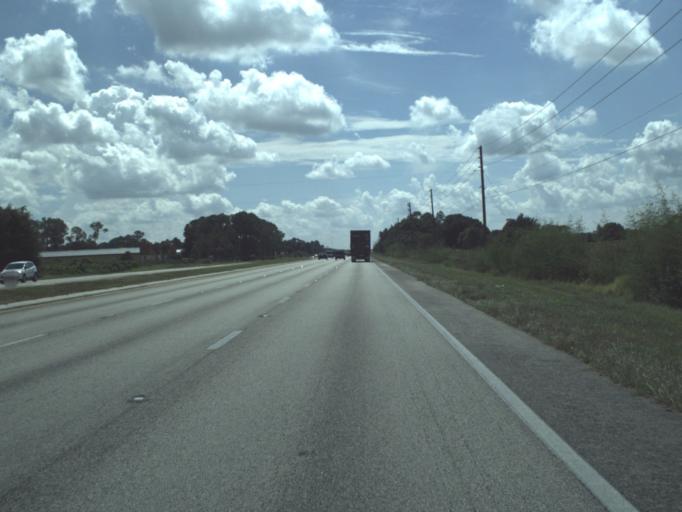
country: US
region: Florida
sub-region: Polk County
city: Lake Wales
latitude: 27.9439
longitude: -81.6152
